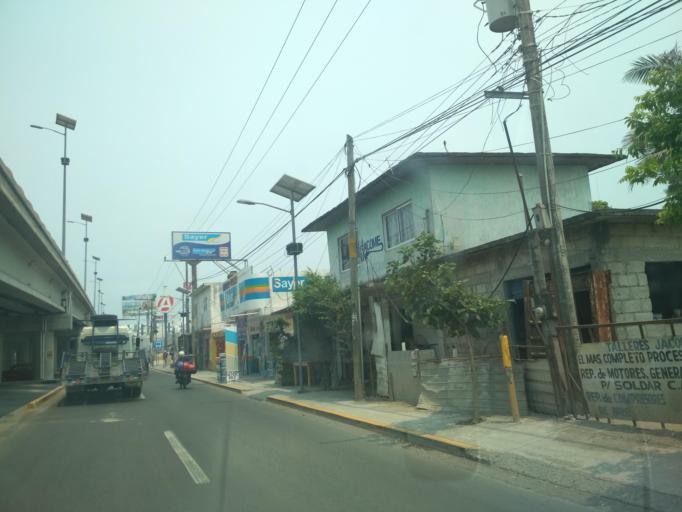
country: MX
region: Veracruz
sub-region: Veracruz
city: Las Amapolas
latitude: 19.1591
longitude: -96.1979
